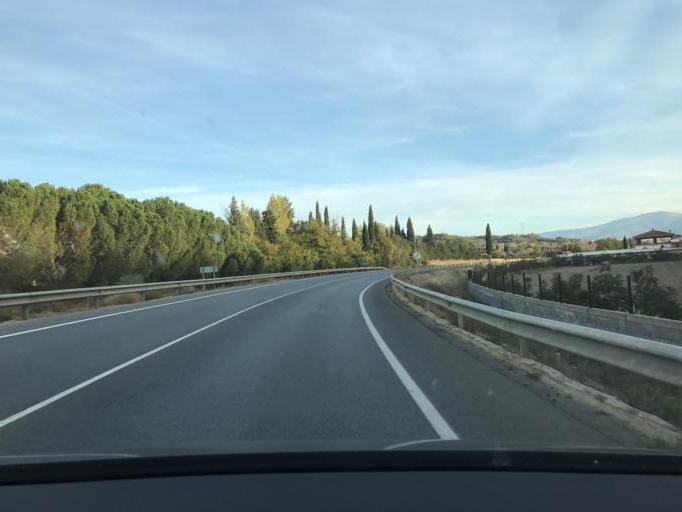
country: ES
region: Andalusia
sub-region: Provincia de Granada
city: Guadix
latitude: 37.2848
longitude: -3.1168
